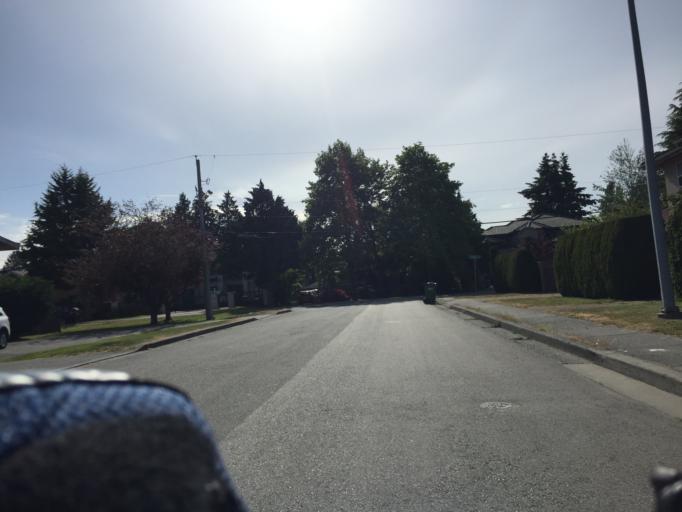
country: CA
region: British Columbia
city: Richmond
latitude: 49.1524
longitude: -123.1337
